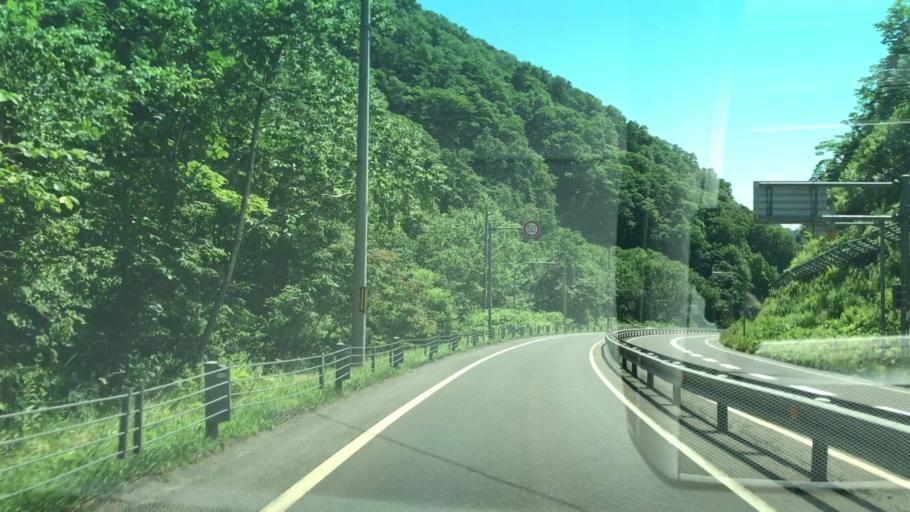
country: JP
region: Hokkaido
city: Yoichi
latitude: 43.0450
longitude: 140.6814
